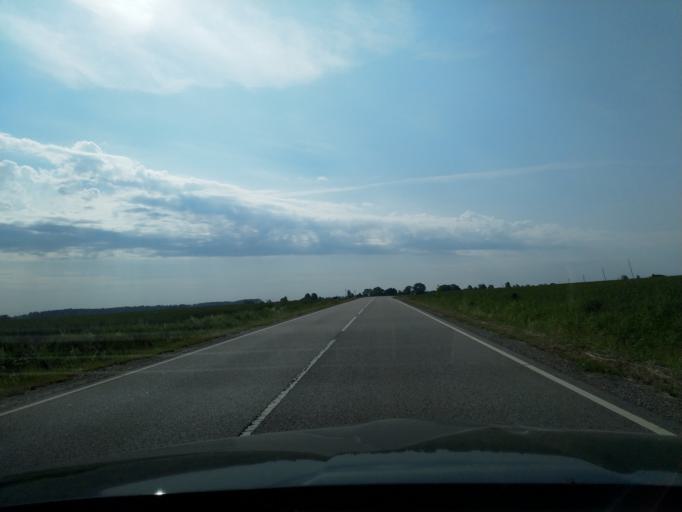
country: LV
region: Talsu Rajons
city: Sabile
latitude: 56.9429
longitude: 22.4872
